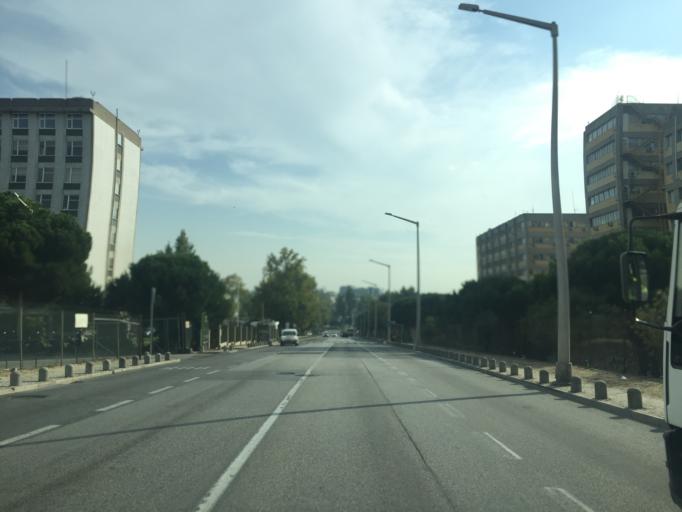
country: PT
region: Lisbon
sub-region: Loures
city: Sacavem
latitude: 38.7767
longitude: -9.1267
